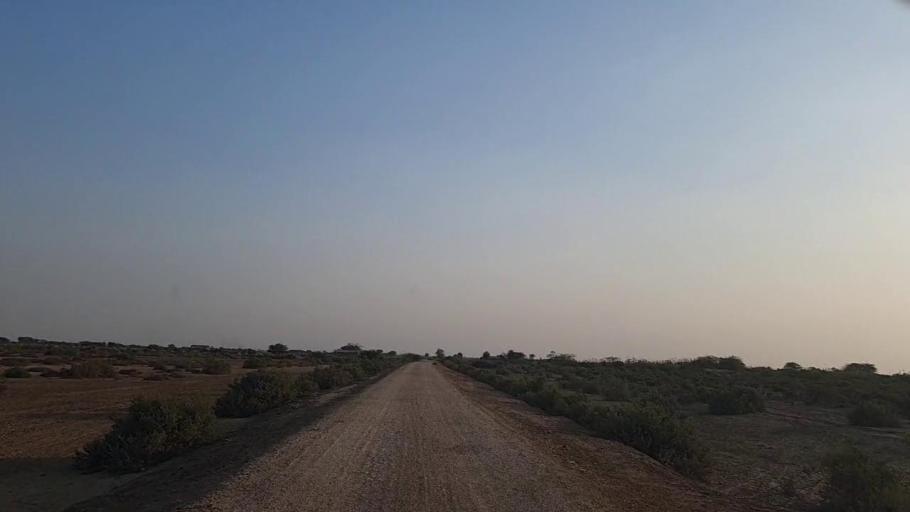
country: PK
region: Sindh
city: Jati
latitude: 24.4883
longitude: 68.4152
